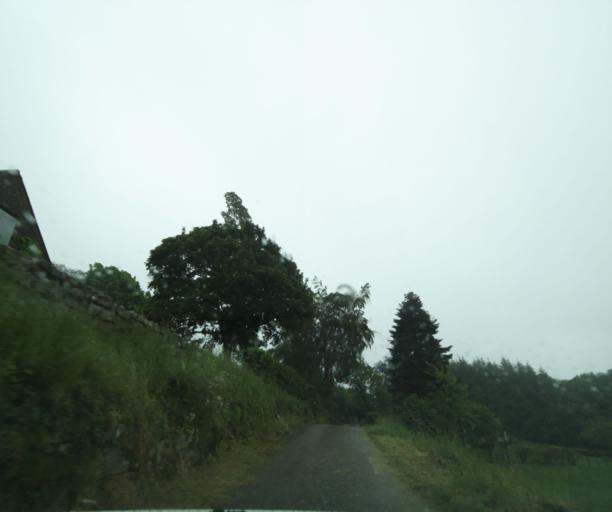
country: FR
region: Bourgogne
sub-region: Departement de Saone-et-Loire
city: La Clayette
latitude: 46.3643
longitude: 4.3503
